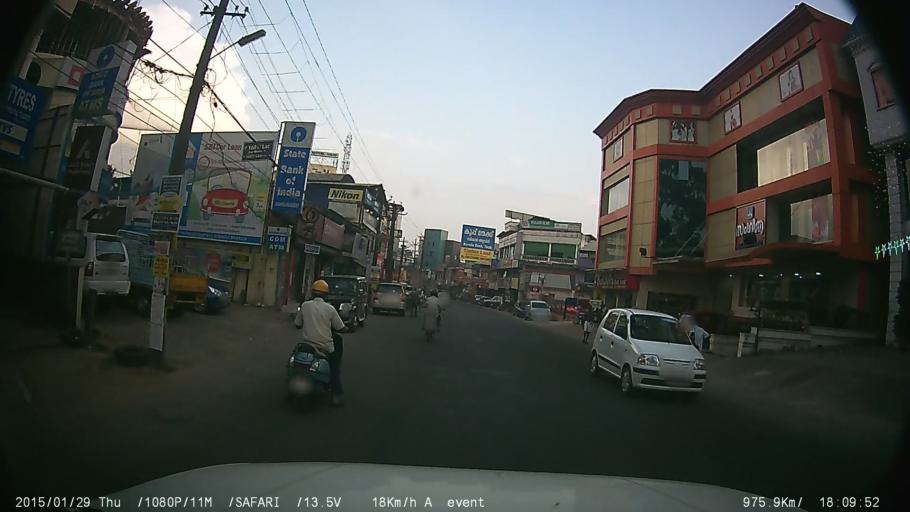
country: IN
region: Kerala
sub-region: Kottayam
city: Changanacheri
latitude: 9.4481
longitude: 76.5393
